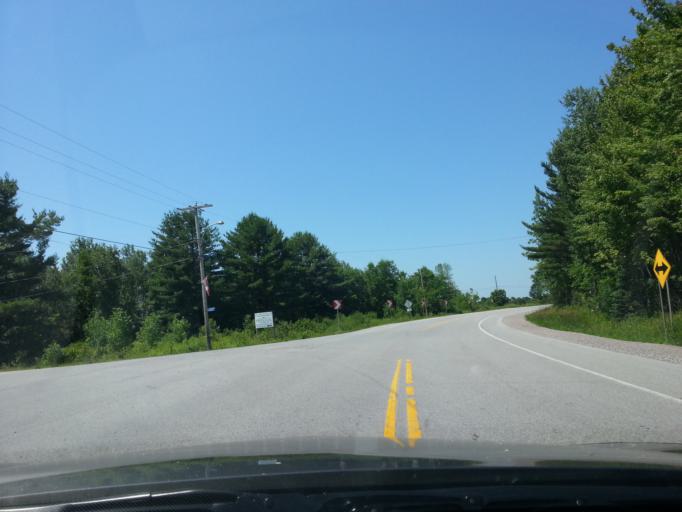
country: CA
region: Ontario
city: Arnprior
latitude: 45.5451
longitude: -76.3651
